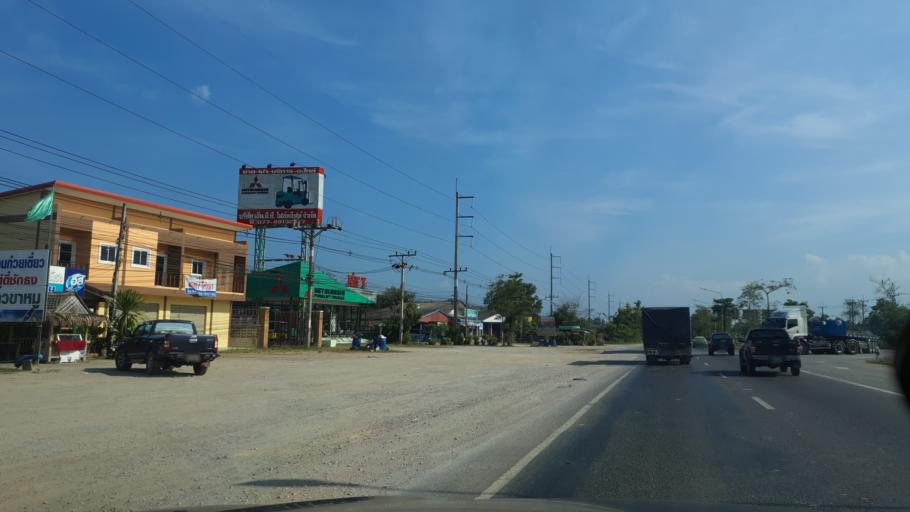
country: TH
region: Surat Thani
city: Phunphin
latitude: 9.0963
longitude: 99.1640
